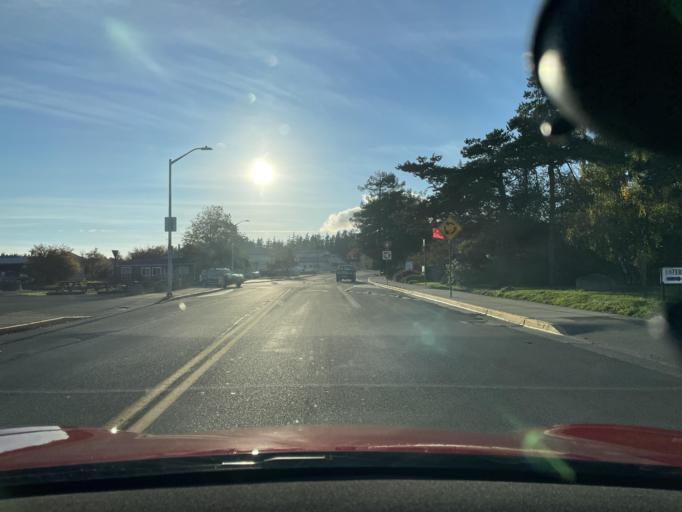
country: US
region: Washington
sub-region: San Juan County
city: Friday Harbor
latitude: 48.5318
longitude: -123.0216
